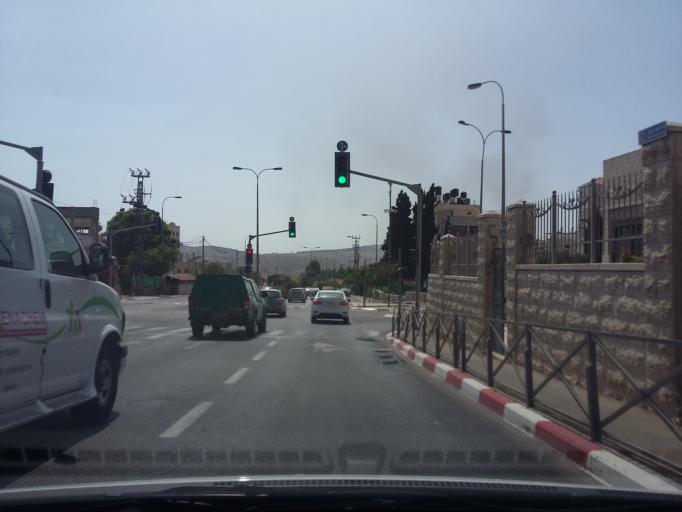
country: PS
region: West Bank
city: Ar Ram wa Dahiyat al Barid
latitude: 31.8297
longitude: 35.2236
